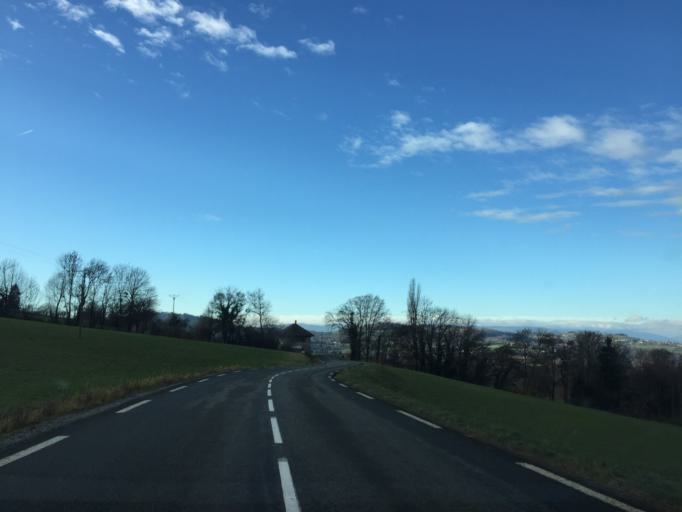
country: FR
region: Rhone-Alpes
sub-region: Departement de la Haute-Savoie
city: Cusy
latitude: 45.7631
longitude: 6.0504
